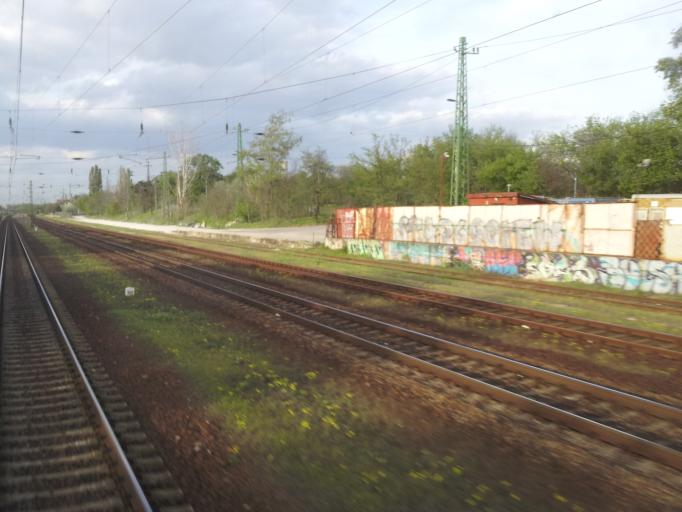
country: HU
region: Pest
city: Dunakeszi
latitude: 47.6206
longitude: 19.1340
